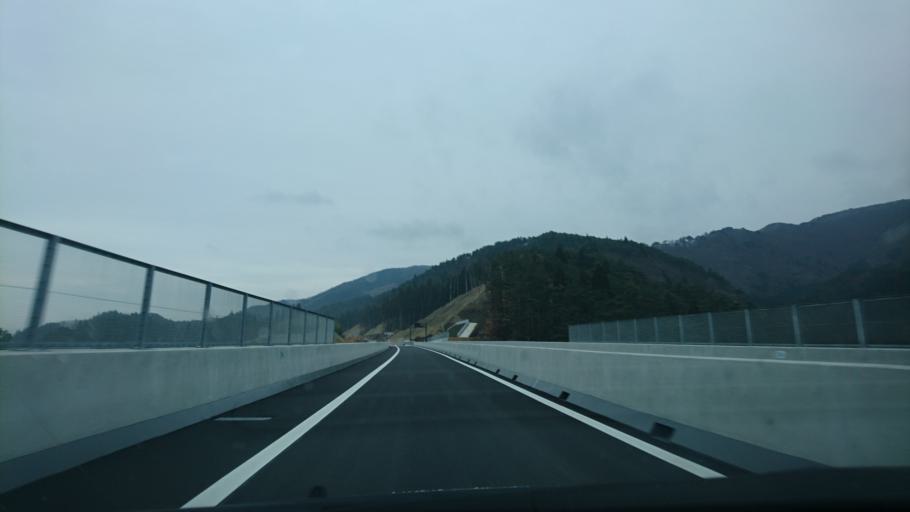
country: JP
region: Iwate
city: Ofunato
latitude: 38.9652
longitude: 141.6243
